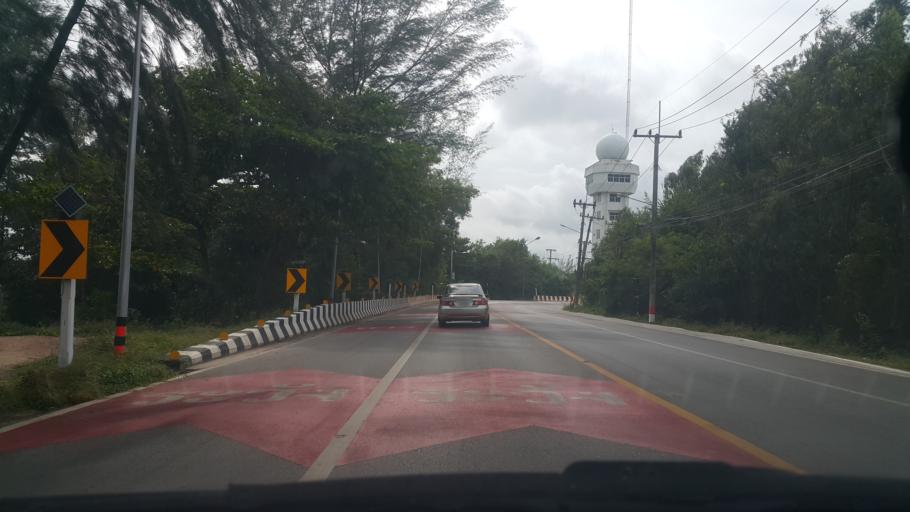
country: TH
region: Rayong
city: Rayong
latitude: 12.6326
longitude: 101.3417
